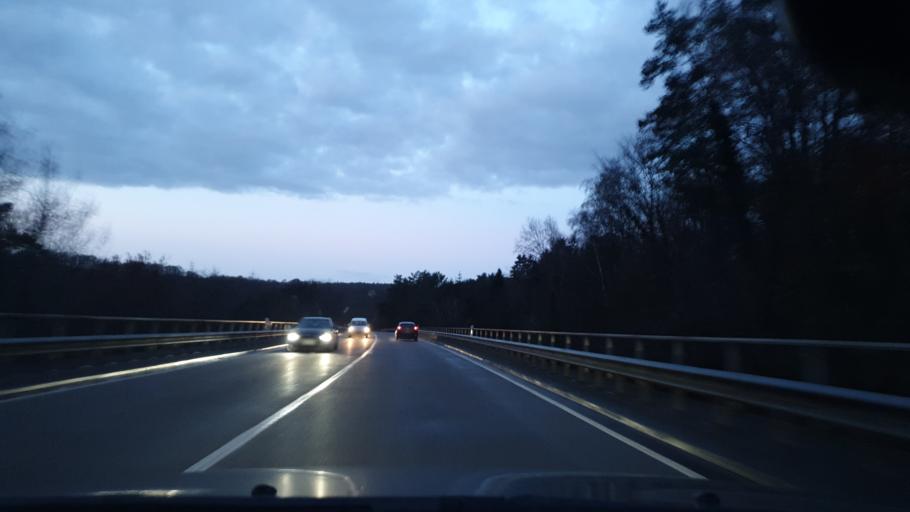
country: DE
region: Rheinland-Pfalz
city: Schopp
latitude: 49.3546
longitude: 7.6866
